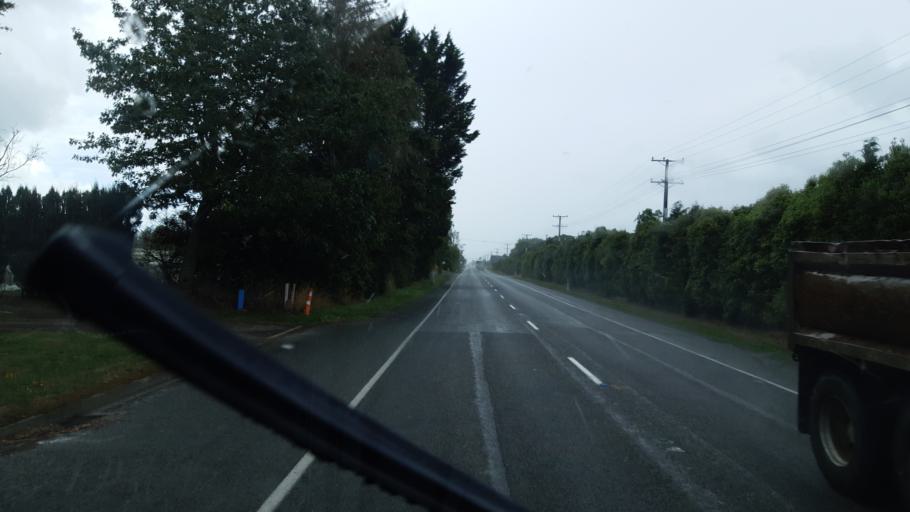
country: NZ
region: Tasman
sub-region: Tasman District
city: Brightwater
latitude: -41.3677
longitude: 173.1322
